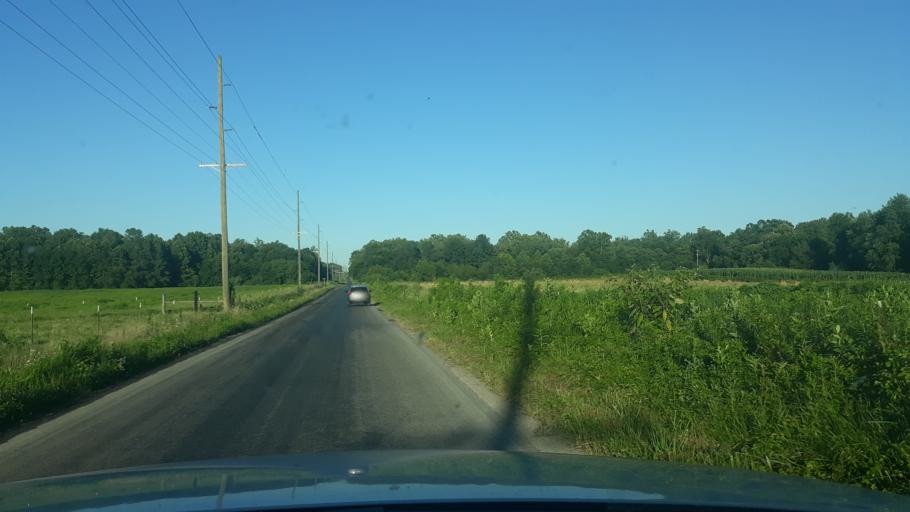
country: US
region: Illinois
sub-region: Saline County
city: Harrisburg
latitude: 37.8632
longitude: -88.5840
